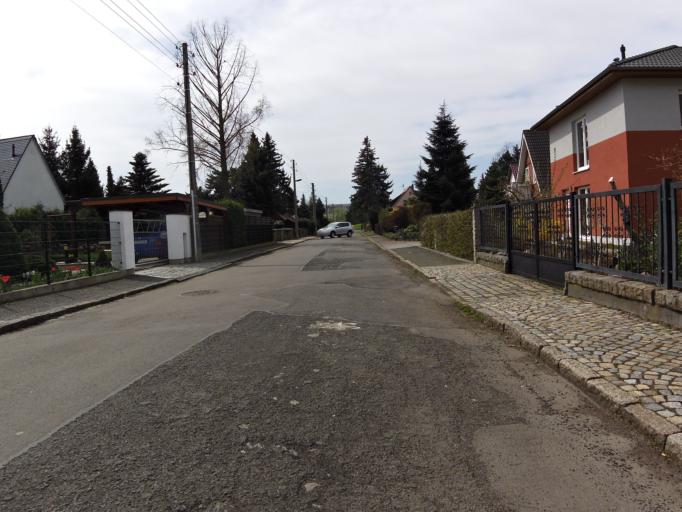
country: DE
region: Saxony
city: Markranstadt
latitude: 51.3158
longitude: 12.2738
